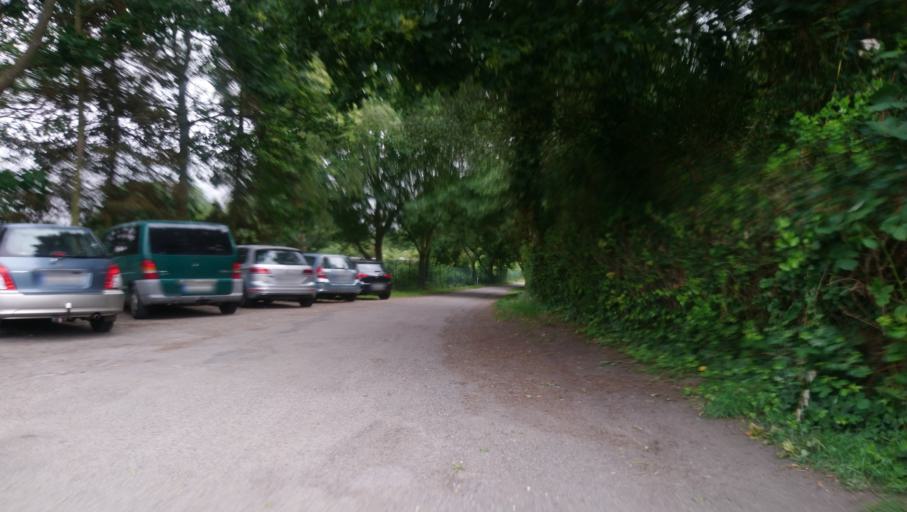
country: DE
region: Mecklenburg-Vorpommern
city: Rostock
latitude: 54.0720
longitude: 12.1001
